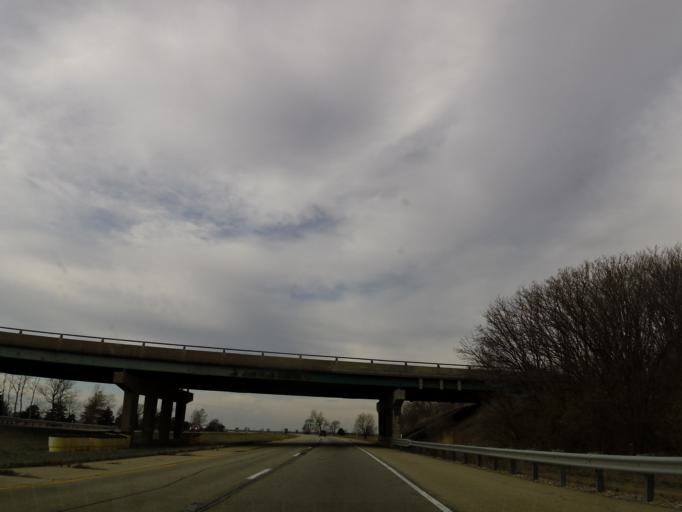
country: US
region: Illinois
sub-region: Peoria County
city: Elmwood
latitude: 40.8510
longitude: -89.9268
